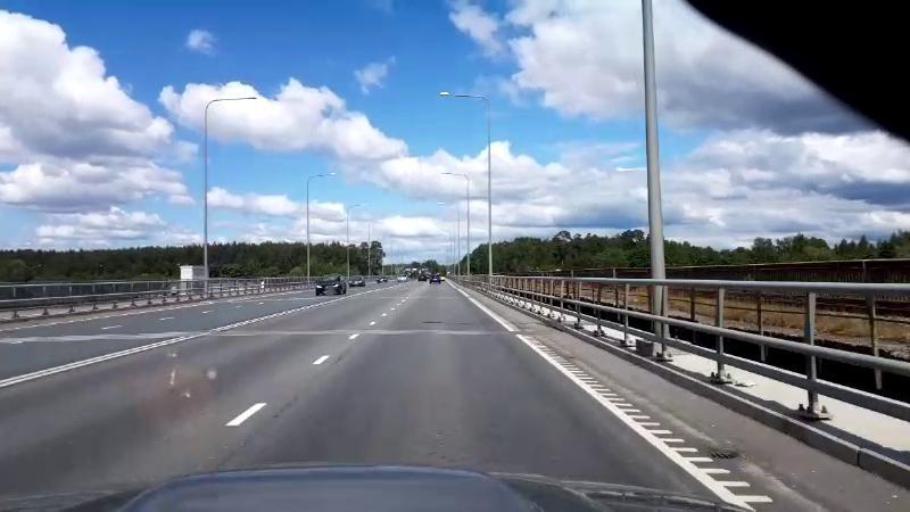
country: EE
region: Paernumaa
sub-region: Paernu linn
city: Parnu
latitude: 58.3782
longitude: 24.5556
